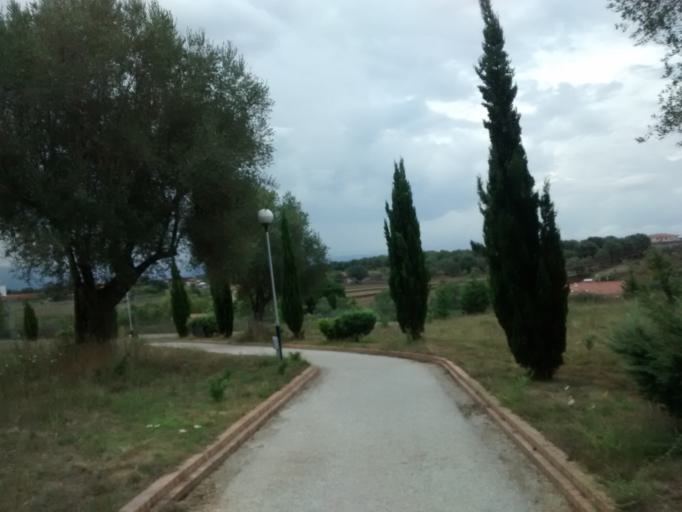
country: IT
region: Calabria
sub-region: Provincia di Vibo-Valentia
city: Vibo Valentia
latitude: 38.6631
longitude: 16.0769
